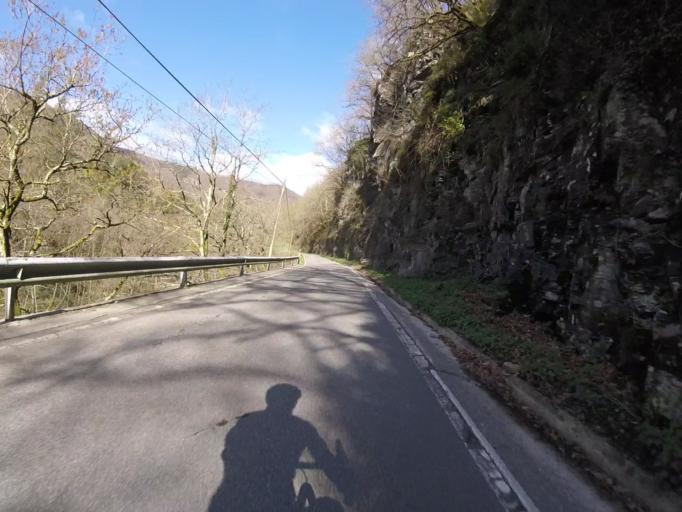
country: ES
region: Navarre
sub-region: Provincia de Navarra
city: Goizueta
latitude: 43.1427
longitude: -1.8484
